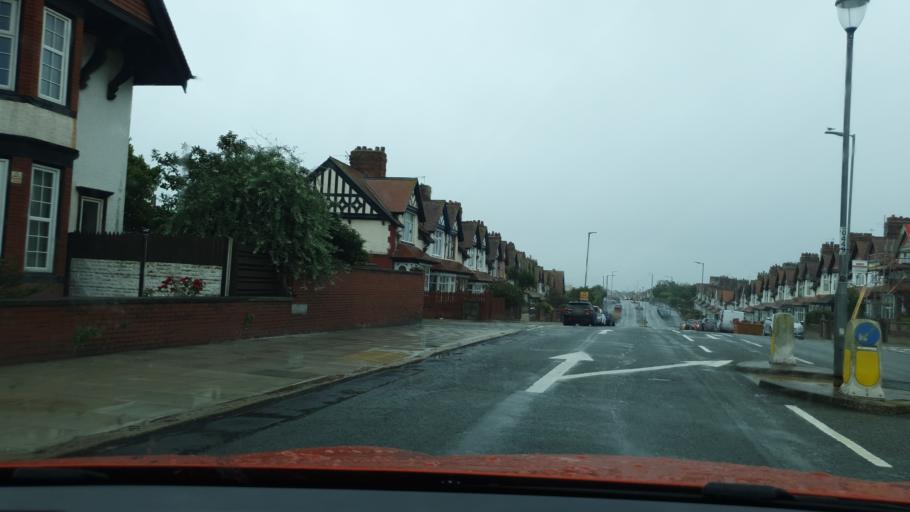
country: GB
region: England
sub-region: Cumbria
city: Barrow in Furness
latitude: 54.1040
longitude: -3.2464
